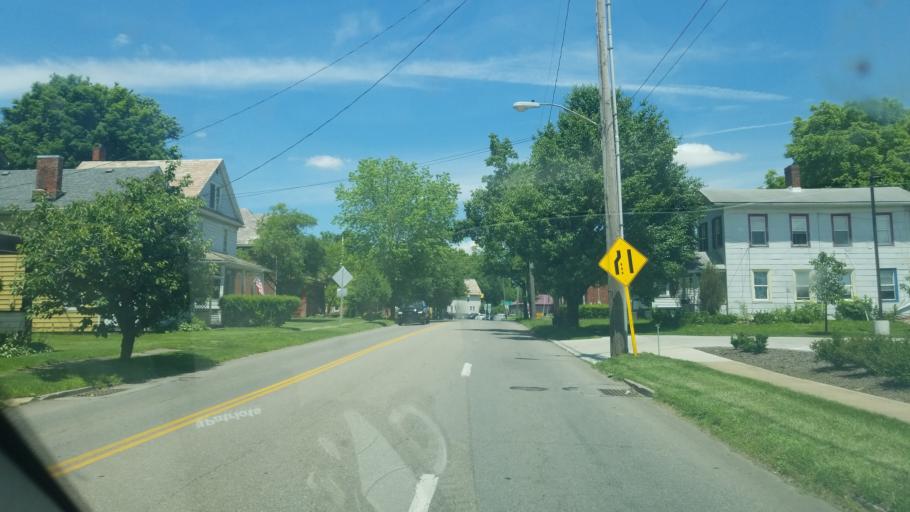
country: US
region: Ohio
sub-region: Columbiana County
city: Lisbon
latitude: 40.7760
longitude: -80.7680
